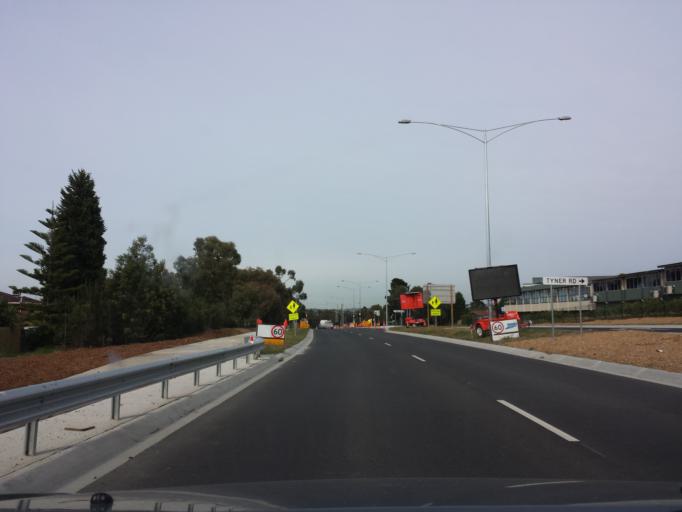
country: AU
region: Victoria
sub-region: Knox
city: Knoxfield
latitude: -37.8745
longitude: 145.2458
